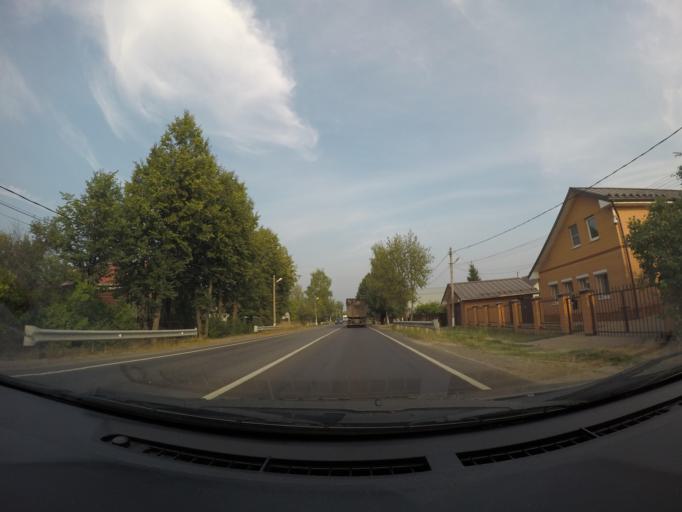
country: RU
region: Moskovskaya
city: Imeni Tsyurupy
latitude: 55.5761
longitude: 38.5893
